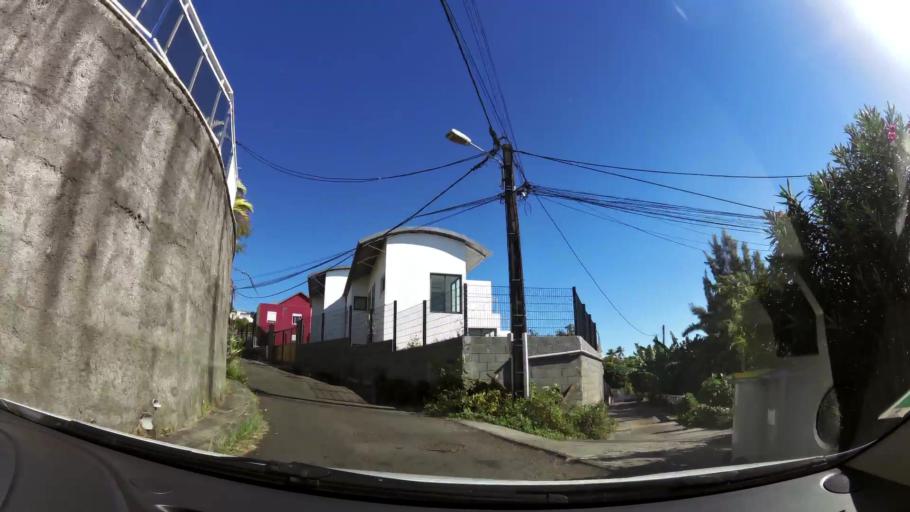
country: RE
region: Reunion
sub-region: Reunion
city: Saint-Denis
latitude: -20.9187
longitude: 55.4831
